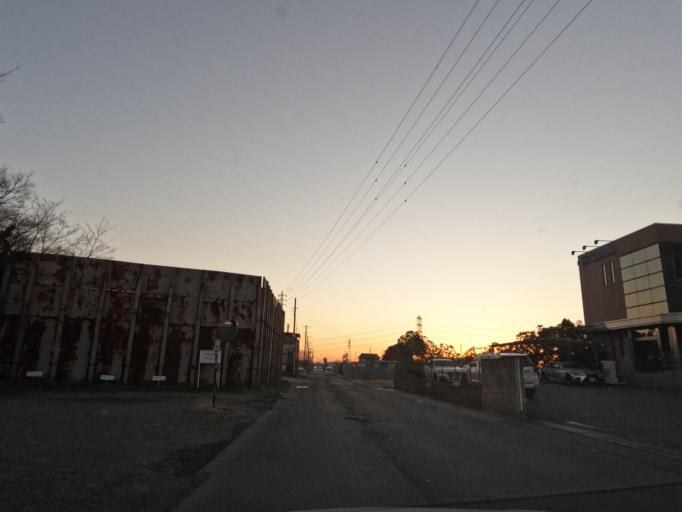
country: JP
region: Saitama
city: Koshigaya
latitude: 35.9212
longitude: 139.7472
